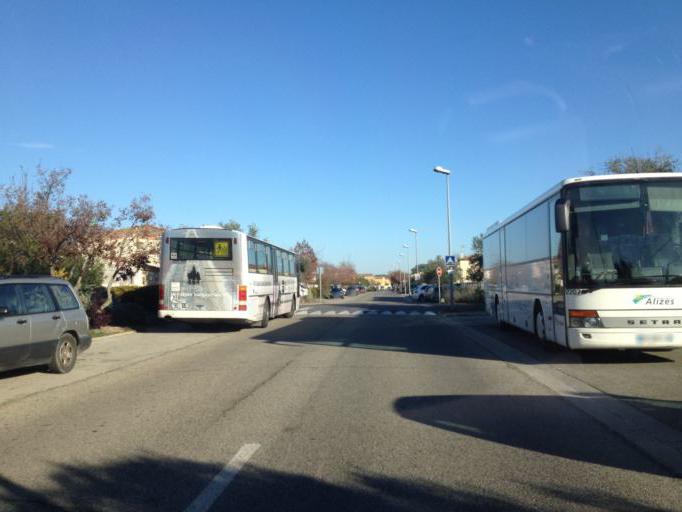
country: FR
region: Provence-Alpes-Cote d'Azur
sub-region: Departement des Bouches-du-Rhone
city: Istres
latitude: 43.5019
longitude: 4.9677
